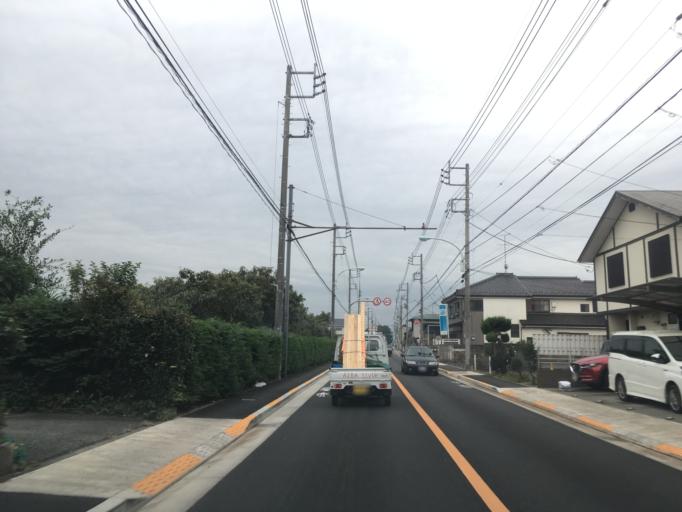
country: JP
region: Tokyo
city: Higashimurayama-shi
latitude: 35.7290
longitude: 139.4657
